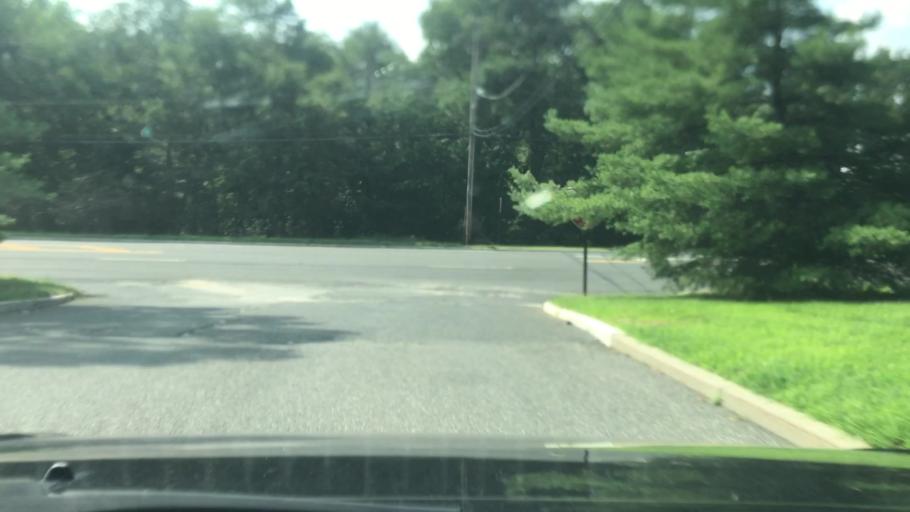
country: US
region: New Jersey
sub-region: Monmouth County
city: Eatontown
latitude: 40.2790
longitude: -74.0692
